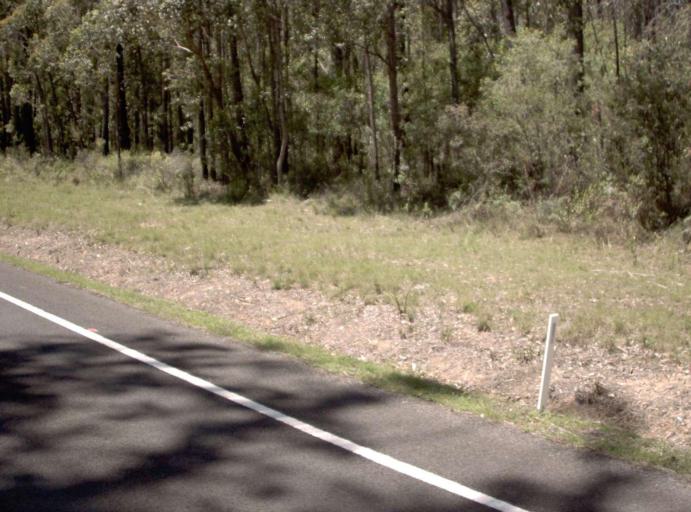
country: AU
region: Victoria
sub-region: East Gippsland
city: Lakes Entrance
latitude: -37.6979
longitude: 148.5883
